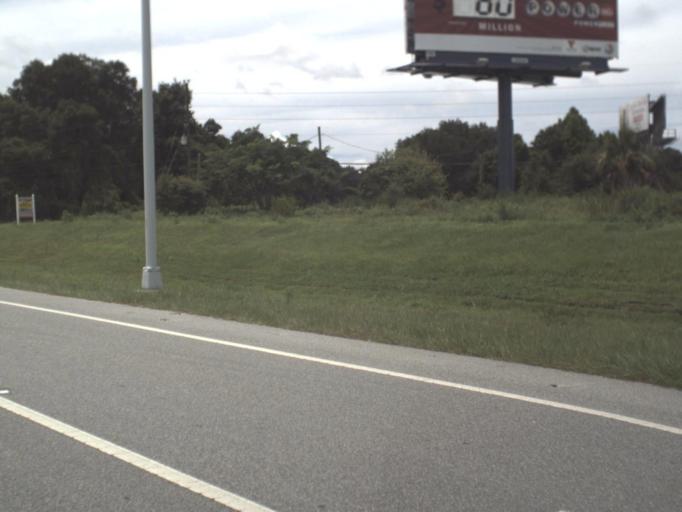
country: US
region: Florida
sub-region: Pasco County
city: Land O' Lakes
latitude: 28.1894
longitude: -82.3991
